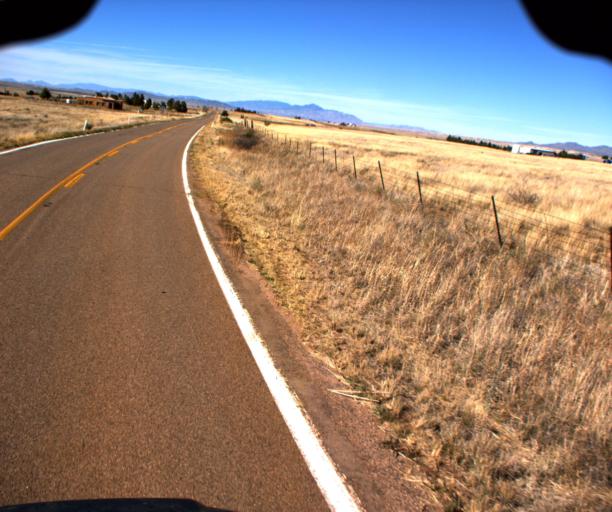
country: US
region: Arizona
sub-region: Cochise County
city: Huachuca City
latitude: 31.6535
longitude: -110.6049
